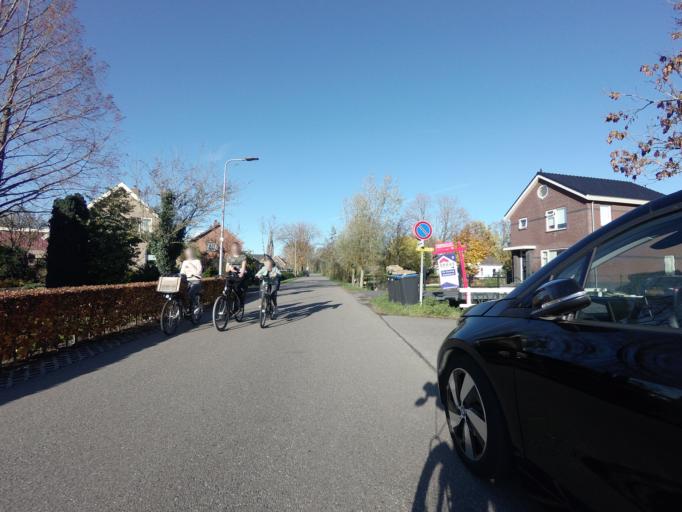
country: NL
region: South Holland
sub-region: Gemeente Nieuwkoop
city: Nieuwkoop
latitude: 52.1465
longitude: 4.7256
